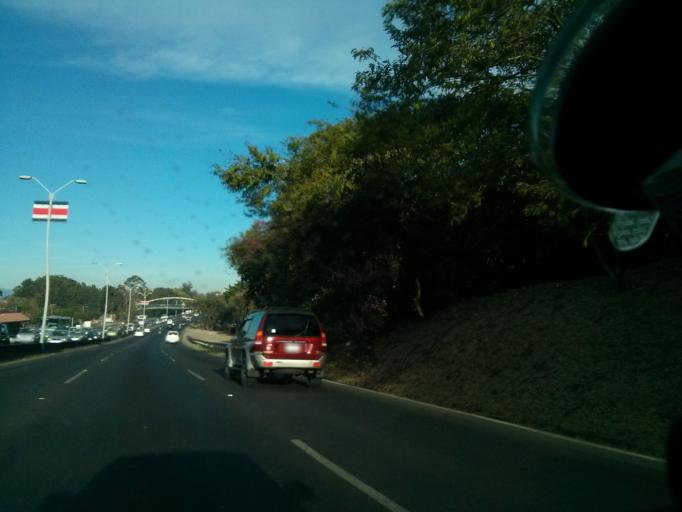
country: CR
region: Heredia
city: La Asuncion
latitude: 9.9738
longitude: -84.1488
